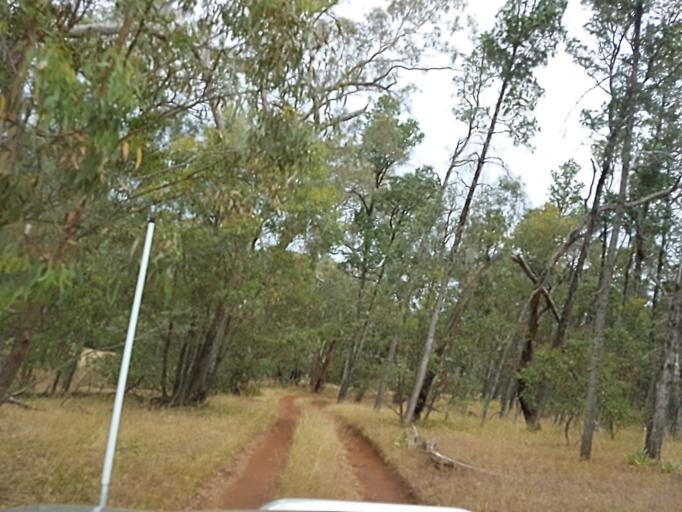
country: AU
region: New South Wales
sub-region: Snowy River
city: Jindabyne
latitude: -36.9328
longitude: 148.4000
